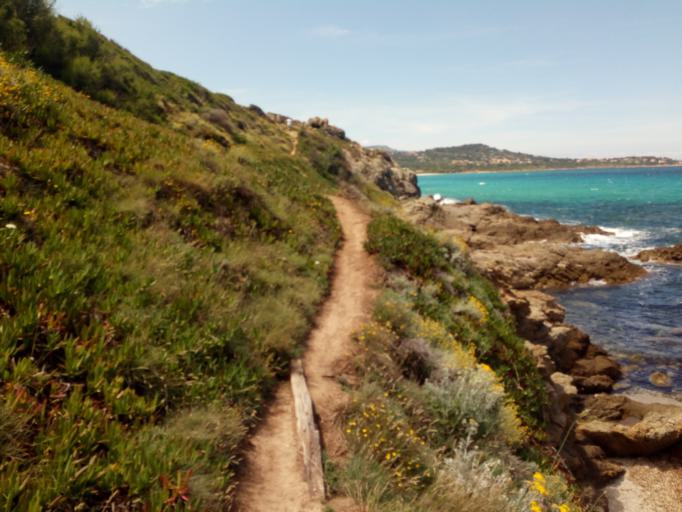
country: FR
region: Corsica
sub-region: Departement de la Haute-Corse
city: L'Ile-Rousse
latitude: 42.6333
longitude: 8.9160
